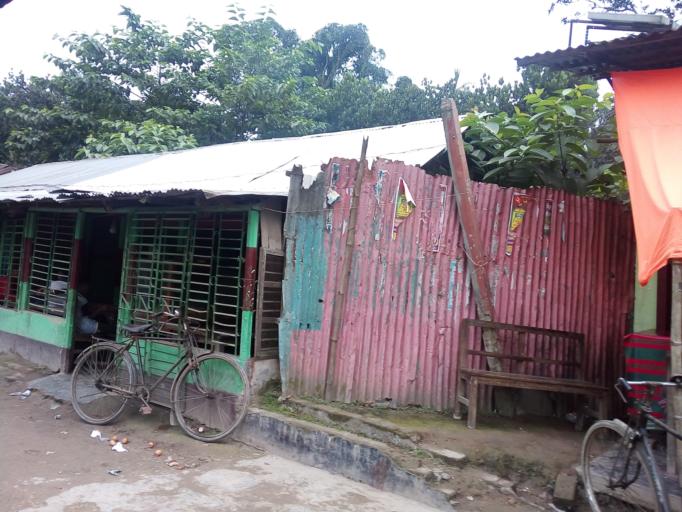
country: BD
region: Rangpur Division
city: Nageswari
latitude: 25.8915
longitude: 89.7099
